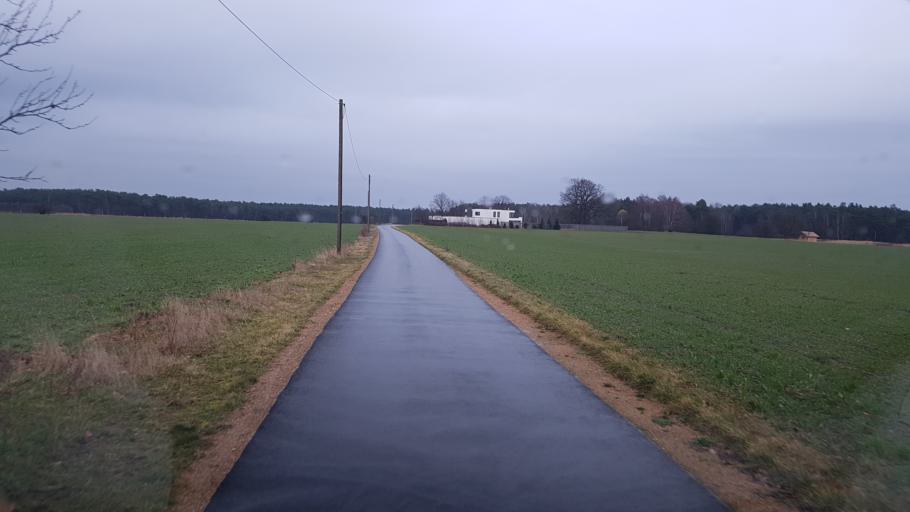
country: DE
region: Brandenburg
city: Sallgast
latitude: 51.6105
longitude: 13.8052
